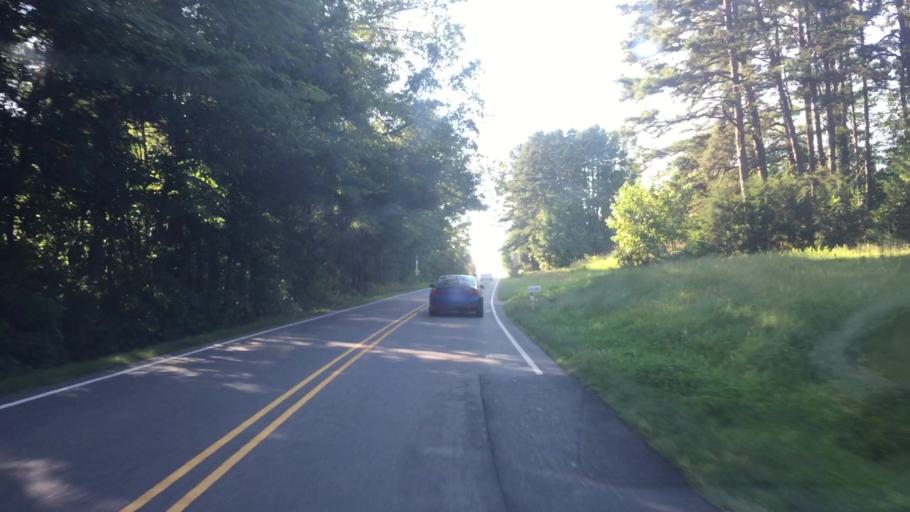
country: US
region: North Carolina
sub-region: Iredell County
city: Mooresville
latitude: 35.5559
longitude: -80.7831
